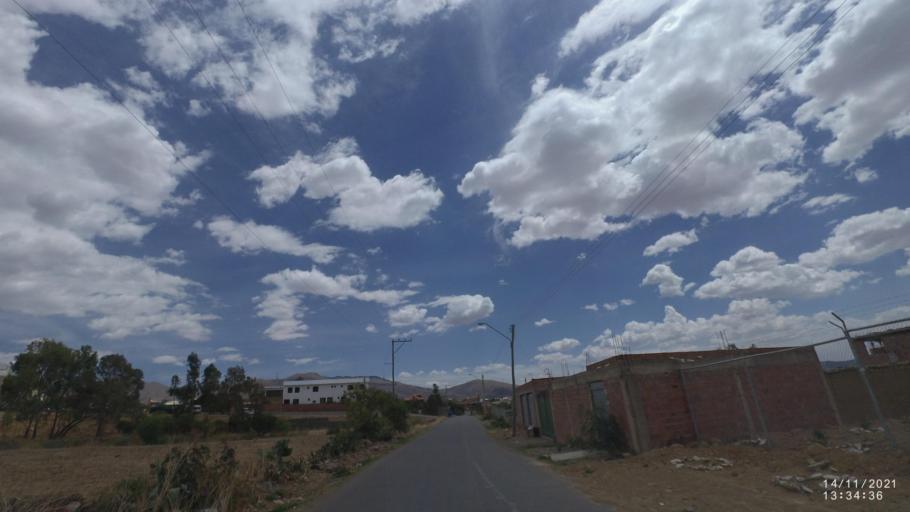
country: BO
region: Cochabamba
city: Colomi
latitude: -17.4034
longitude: -65.9849
